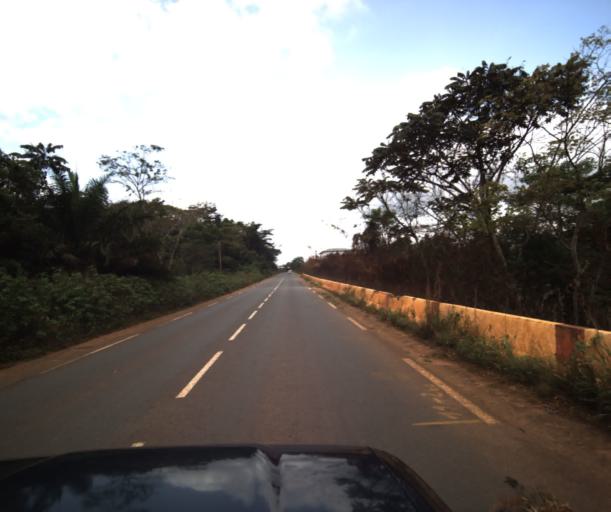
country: CM
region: Centre
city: Mbankomo
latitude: 3.7915
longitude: 11.4152
